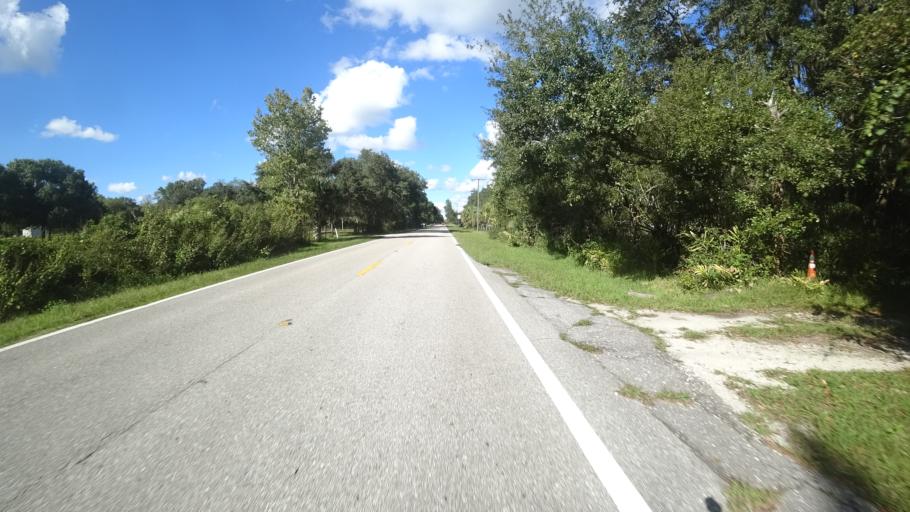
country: US
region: Florida
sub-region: Sarasota County
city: Lake Sarasota
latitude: 27.3079
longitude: -82.2671
